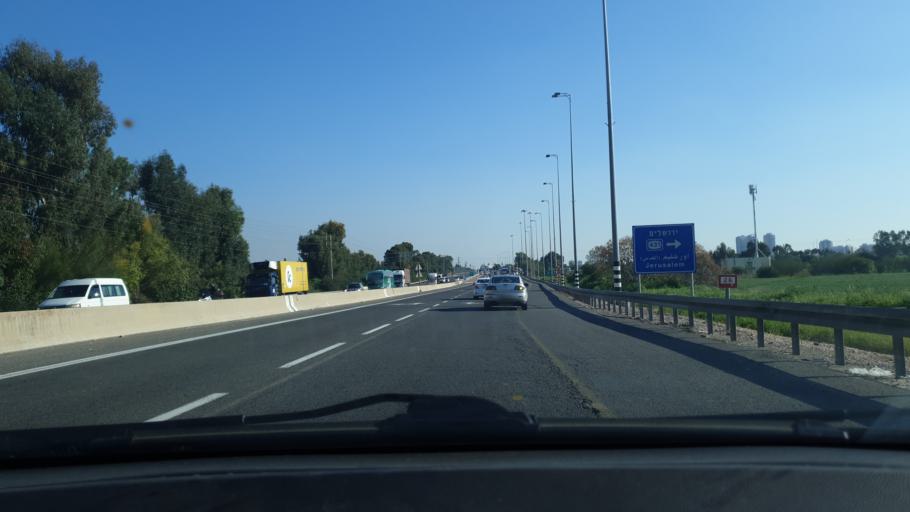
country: IL
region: Central District
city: Ramla
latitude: 31.9553
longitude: 34.8545
